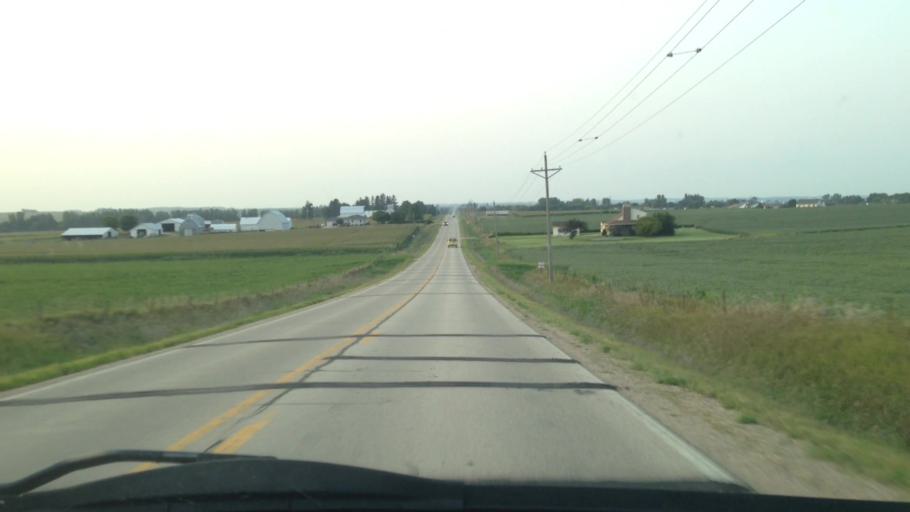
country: US
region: Iowa
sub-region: Benton County
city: Atkins
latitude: 41.9870
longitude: -91.8731
